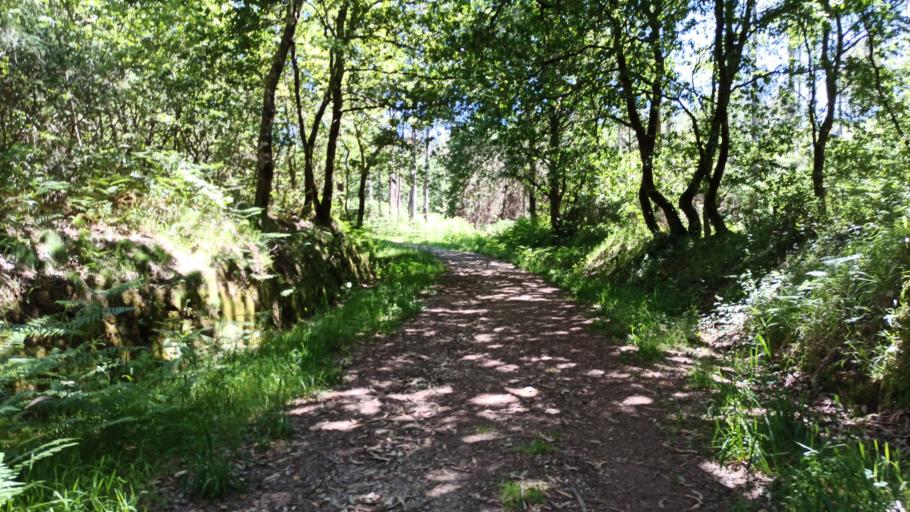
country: ES
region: Galicia
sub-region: Provincia da Coruna
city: Negreira
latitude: 42.9196
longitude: -8.7221
